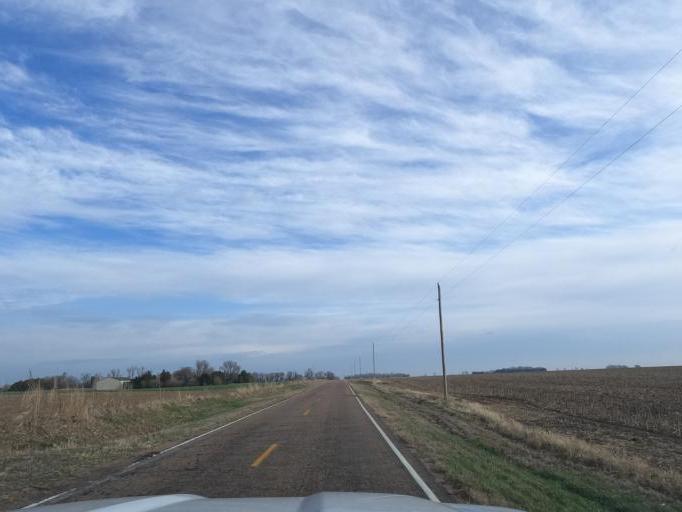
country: US
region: Kansas
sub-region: Rice County
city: Sterling
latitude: 38.1033
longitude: -98.2521
